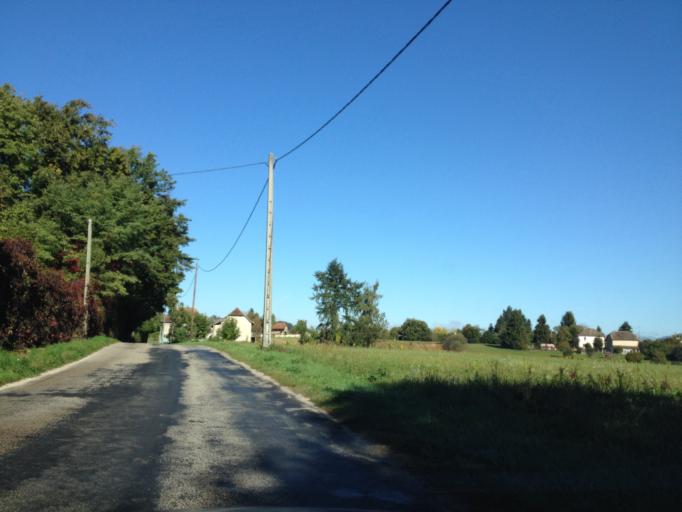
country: FR
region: Rhone-Alpes
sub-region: Departement de l'Isere
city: Morestel
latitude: 45.6527
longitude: 5.4682
